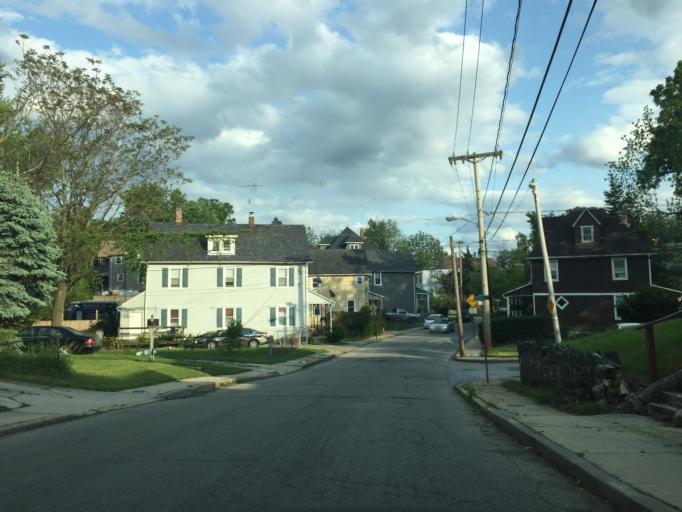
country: US
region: Maryland
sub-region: Baltimore County
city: Rosedale
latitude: 39.3301
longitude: -76.5677
